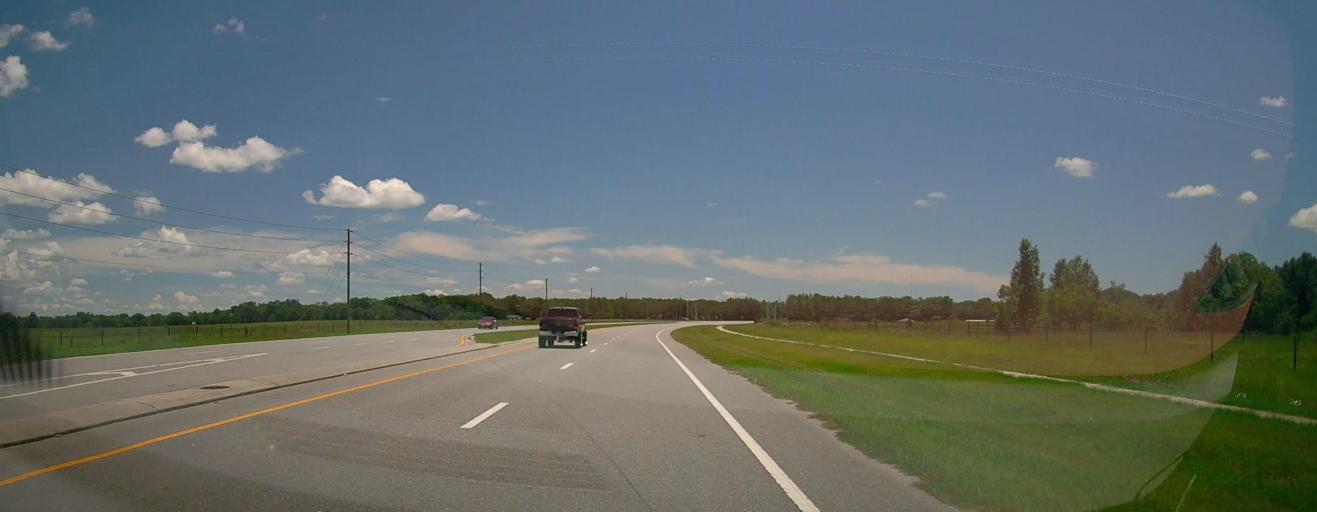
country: US
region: Florida
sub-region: Marion County
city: Silver Springs Shores
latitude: 29.0666
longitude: -82.0208
